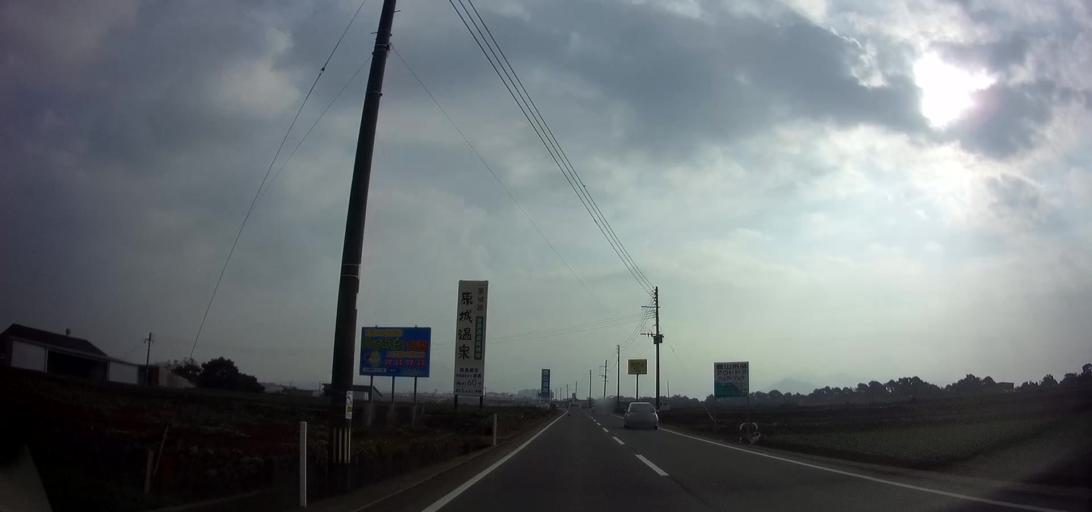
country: JP
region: Nagasaki
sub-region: Isahaya-shi
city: Isahaya
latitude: 32.7973
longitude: 130.1531
